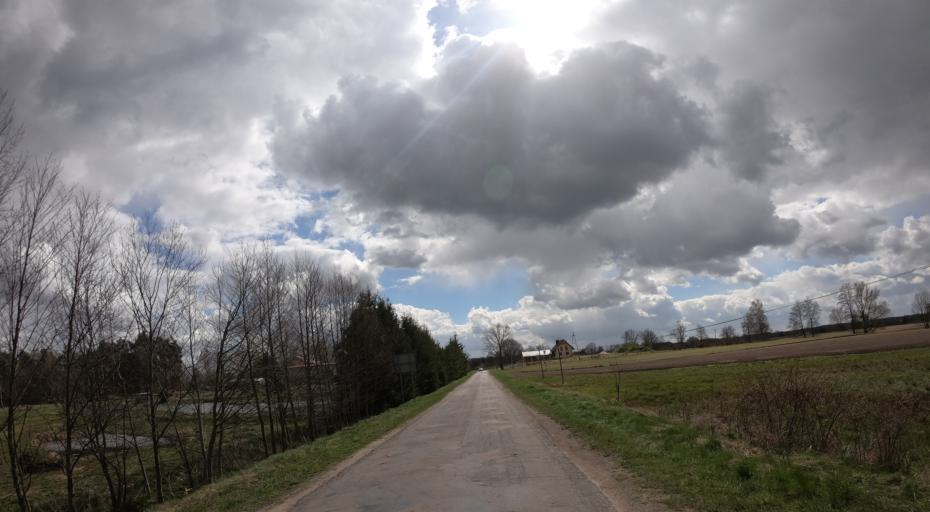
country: PL
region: West Pomeranian Voivodeship
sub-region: Powiat drawski
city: Drawsko Pomorskie
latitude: 53.5288
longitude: 15.8862
